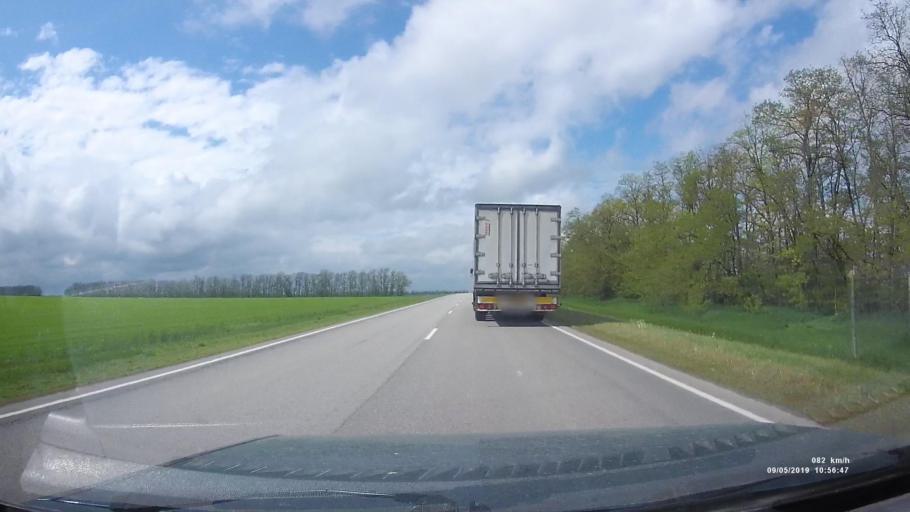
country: RU
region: Rostov
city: Peshkovo
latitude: 46.8680
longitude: 39.2924
